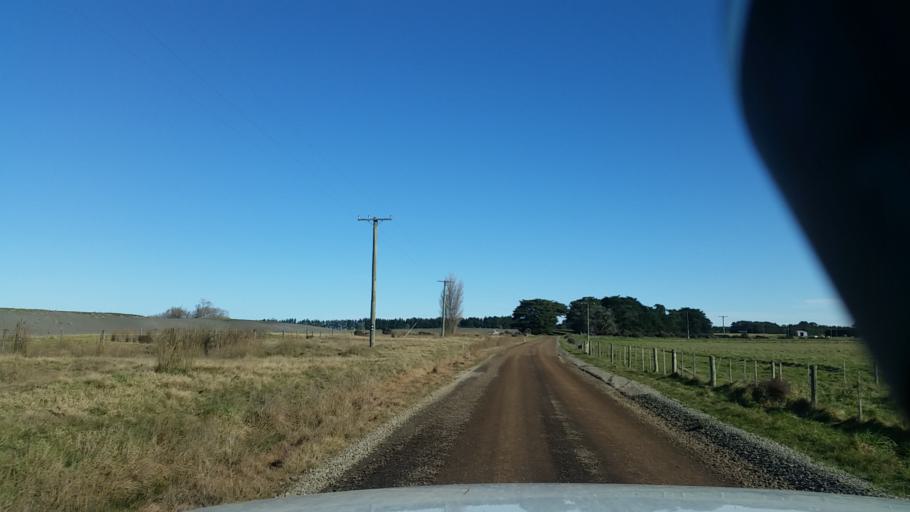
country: NZ
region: Canterbury
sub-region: Selwyn District
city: Lincoln
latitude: -43.8049
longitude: 172.6862
